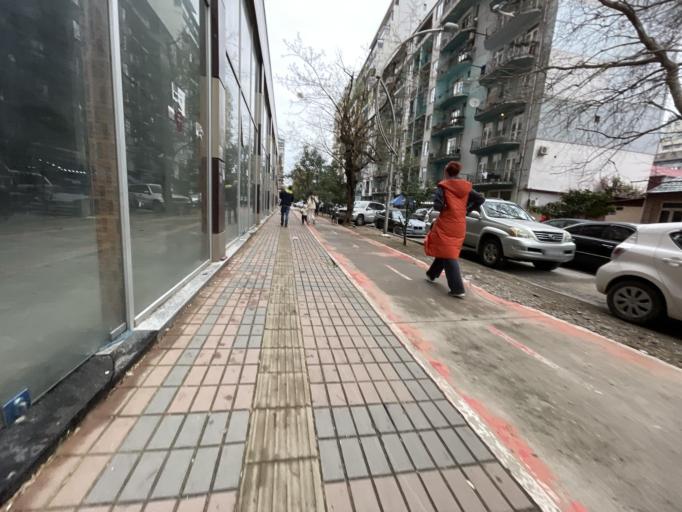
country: GE
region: Ajaria
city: Batumi
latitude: 41.6432
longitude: 41.6290
